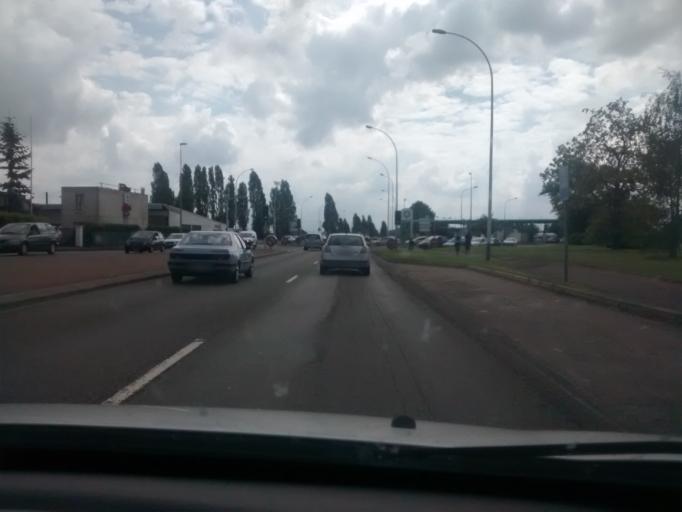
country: FR
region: Ile-de-France
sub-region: Departement des Yvelines
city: Trappes
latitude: 48.7735
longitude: 1.9931
